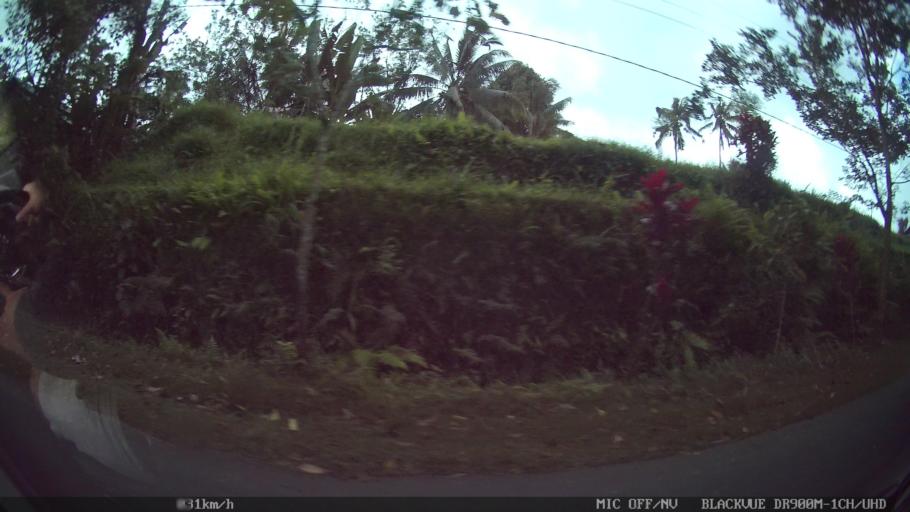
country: ID
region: Bali
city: Banjar Petak
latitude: -8.4391
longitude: 115.3207
